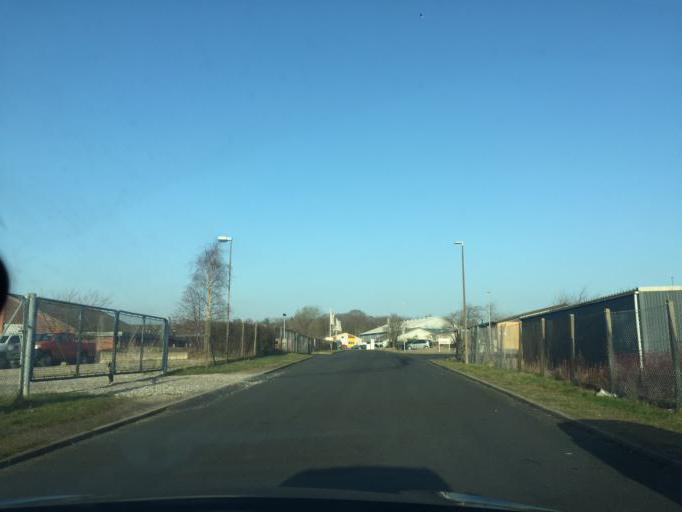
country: DK
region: South Denmark
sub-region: Faaborg-Midtfyn Kommune
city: Faaborg
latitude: 55.1092
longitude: 10.2358
